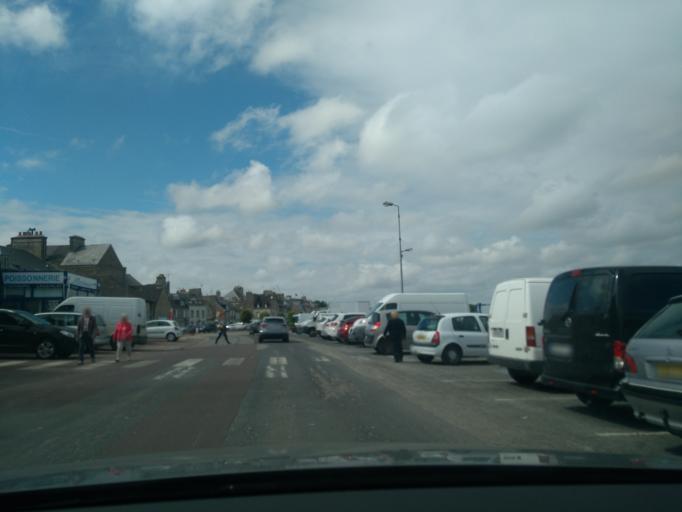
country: FR
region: Lower Normandy
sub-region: Departement de la Manche
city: Saint-Vaast-la-Hougue
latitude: 49.5879
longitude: -1.2655
